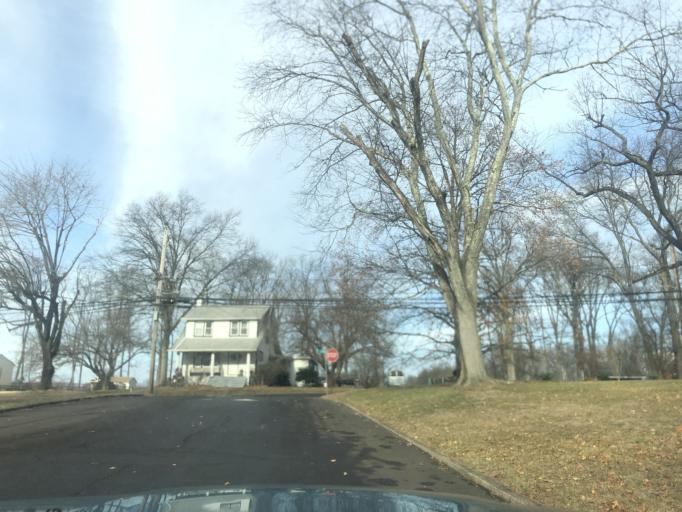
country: US
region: Pennsylvania
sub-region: Bucks County
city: Perkasie
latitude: 40.3835
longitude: -75.2898
